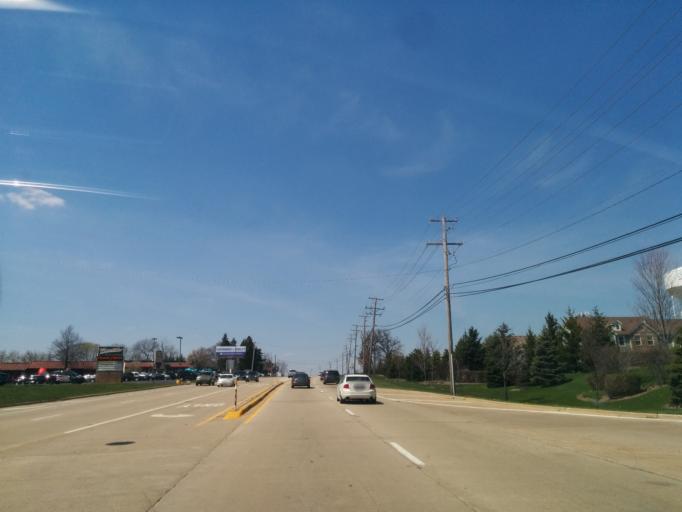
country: US
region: Illinois
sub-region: Cook County
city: Bartlett
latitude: 42.0104
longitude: -88.2096
